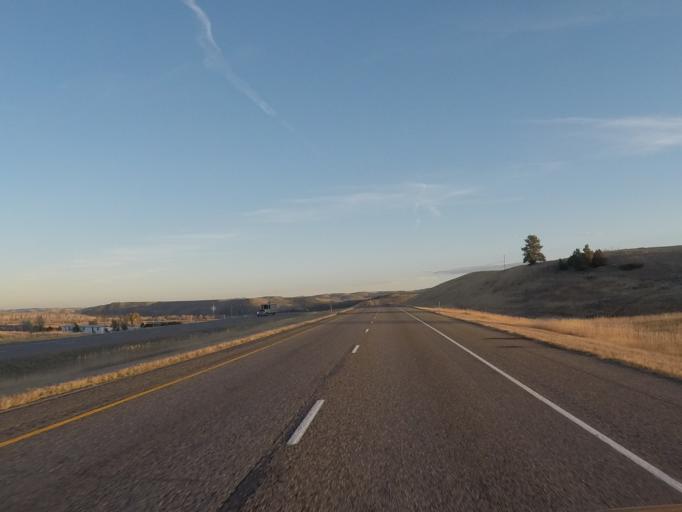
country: US
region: Montana
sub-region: Sweet Grass County
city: Big Timber
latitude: 45.7526
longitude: -109.7793
